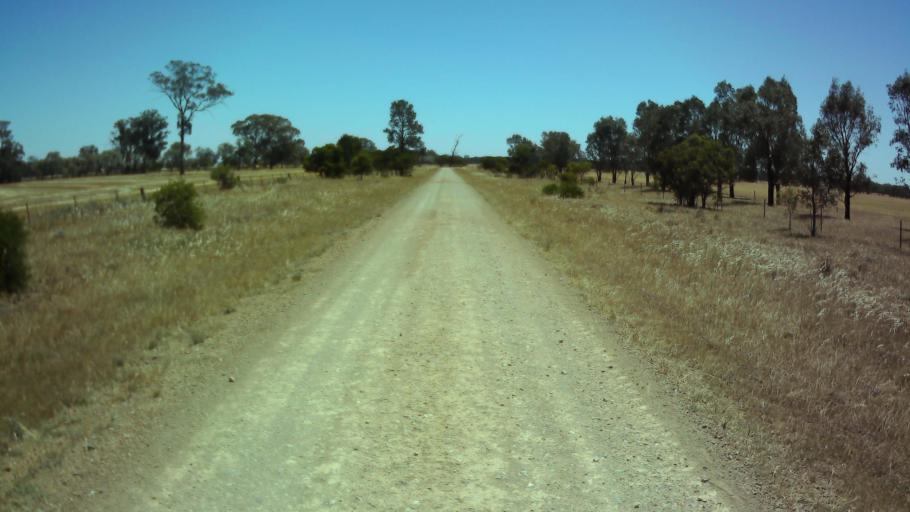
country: AU
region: New South Wales
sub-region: Weddin
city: Grenfell
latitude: -33.9878
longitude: 147.9305
